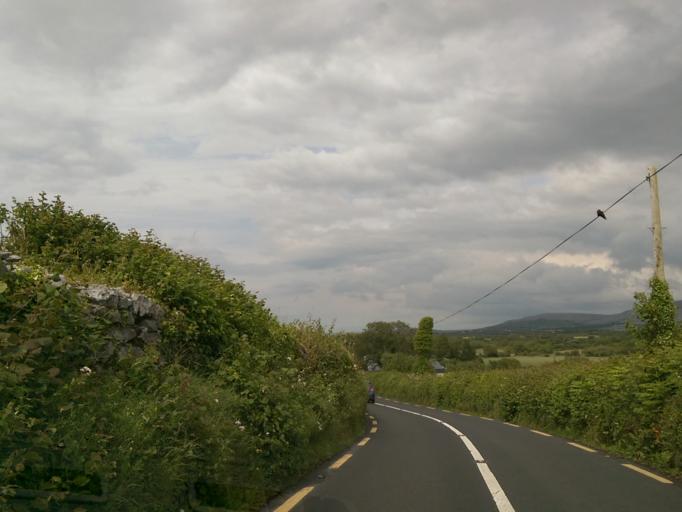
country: IE
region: Connaught
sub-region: County Galway
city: Bearna
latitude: 53.0836
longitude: -9.1800
